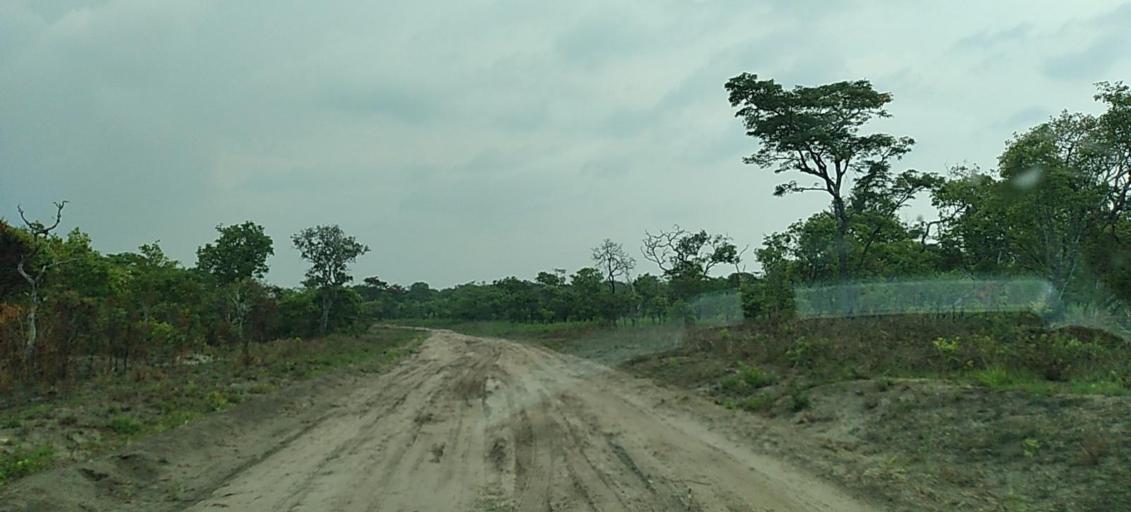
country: ZM
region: North-Western
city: Mwinilunga
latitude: -11.4267
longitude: 24.5921
